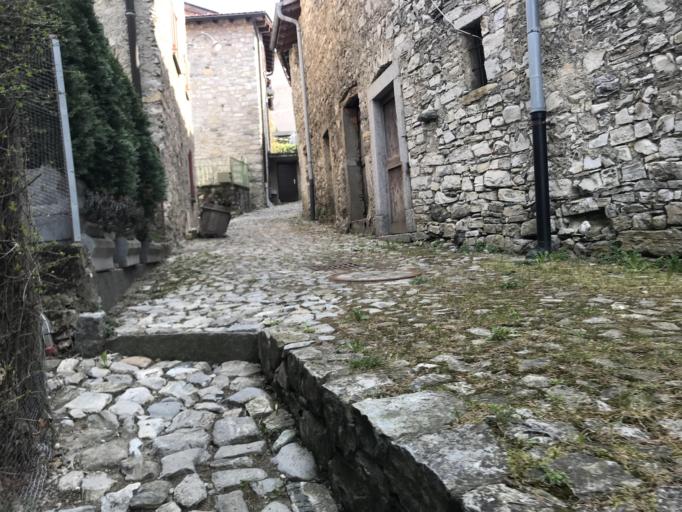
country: CH
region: Ticino
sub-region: Lugano District
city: Pregassona
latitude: 46.0121
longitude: 8.9966
